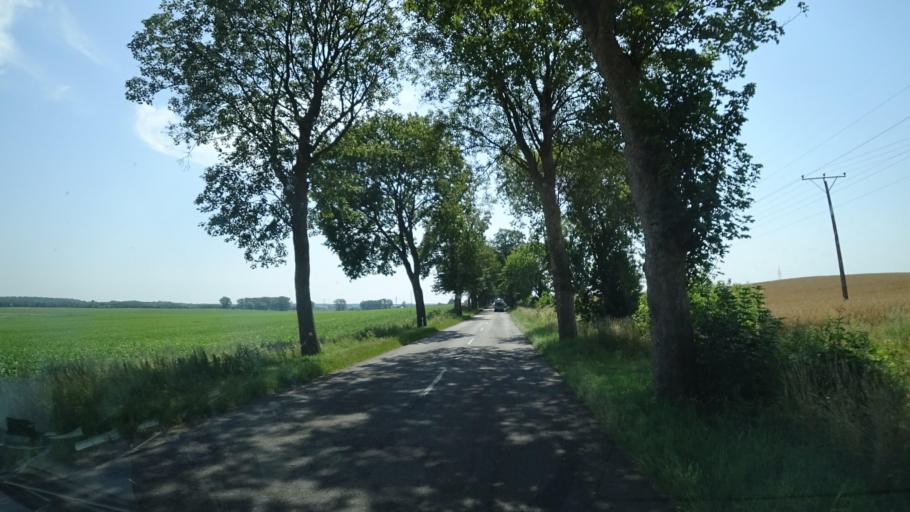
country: PL
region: West Pomeranian Voivodeship
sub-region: Powiat lobeski
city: Lobez
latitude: 53.6590
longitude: 15.6111
